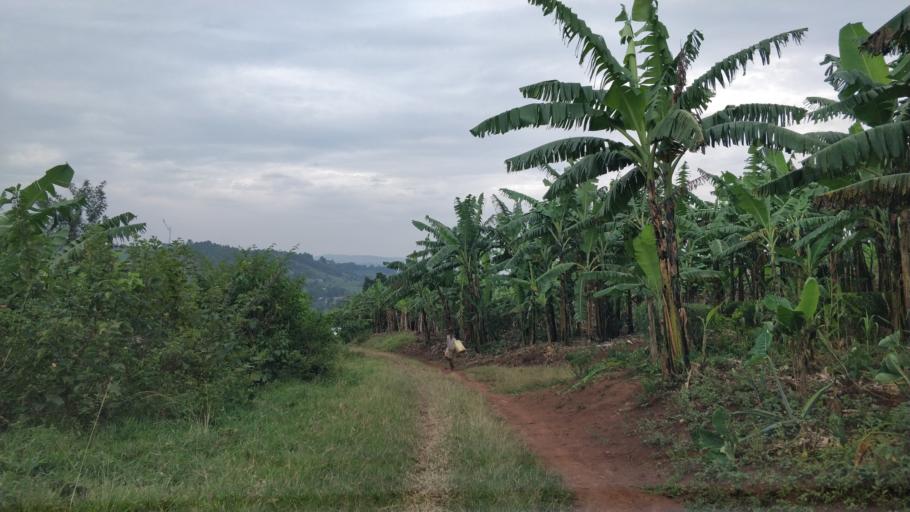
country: UG
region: Western Region
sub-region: Sheema District
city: Kibingo
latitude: -0.7027
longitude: 30.4002
